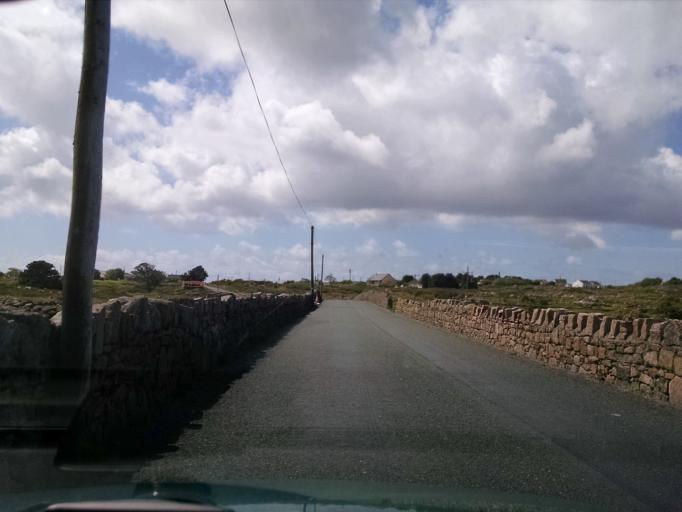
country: IE
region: Connaught
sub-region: County Galway
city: Oughterard
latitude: 53.3027
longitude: -9.6361
